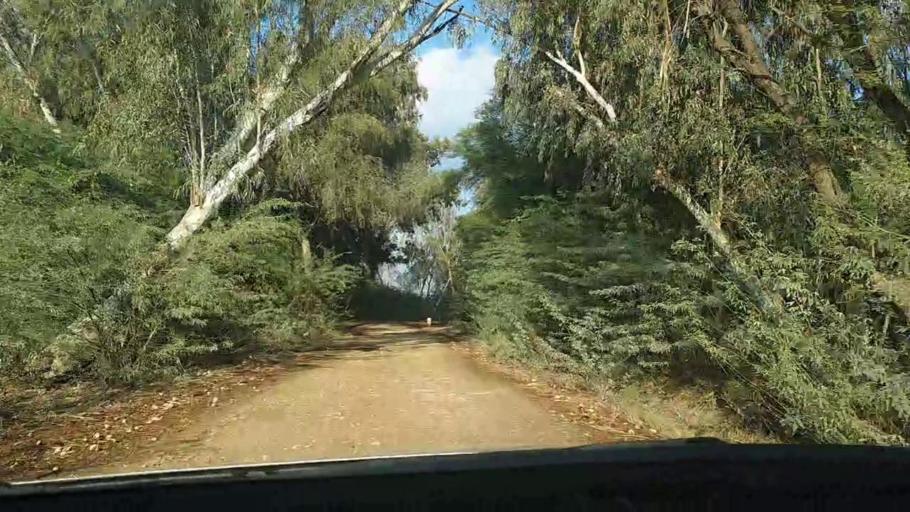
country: PK
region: Sindh
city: Tando Mittha Khan
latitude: 25.9009
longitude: 69.3034
